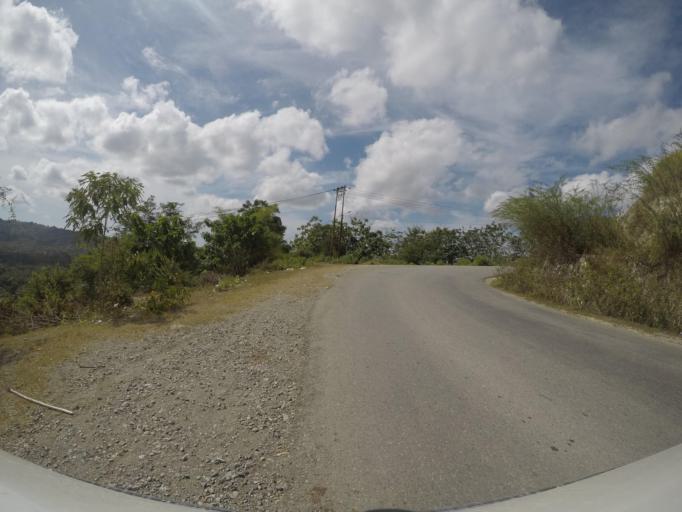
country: TL
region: Viqueque
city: Viqueque
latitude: -8.8720
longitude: 126.3612
